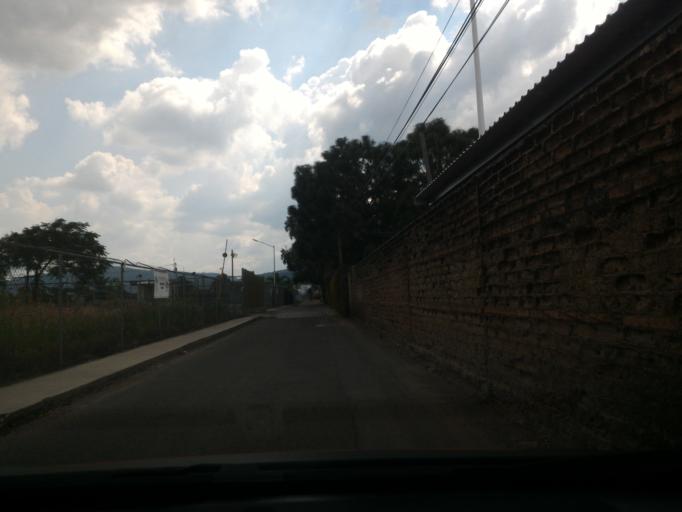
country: MX
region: Jalisco
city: Nuevo Mexico
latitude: 20.7000
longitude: -103.4705
